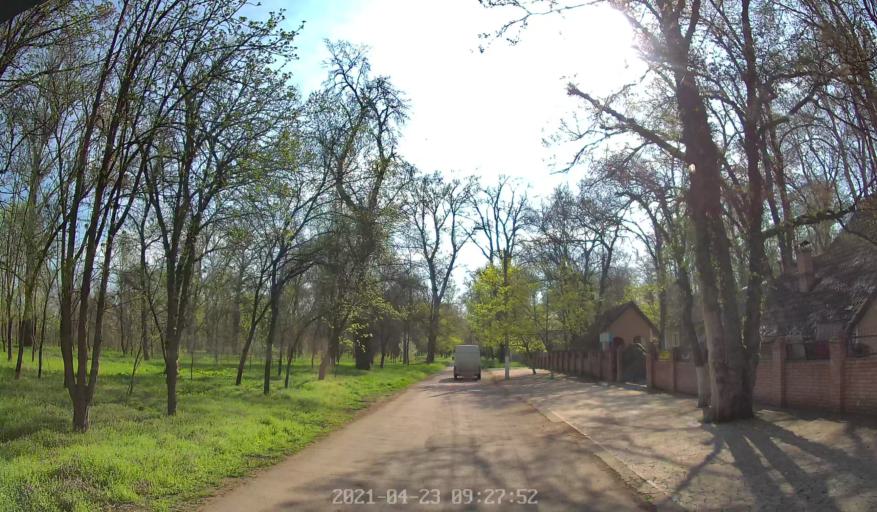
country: MD
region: Chisinau
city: Vadul lui Voda
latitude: 47.0864
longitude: 29.1031
